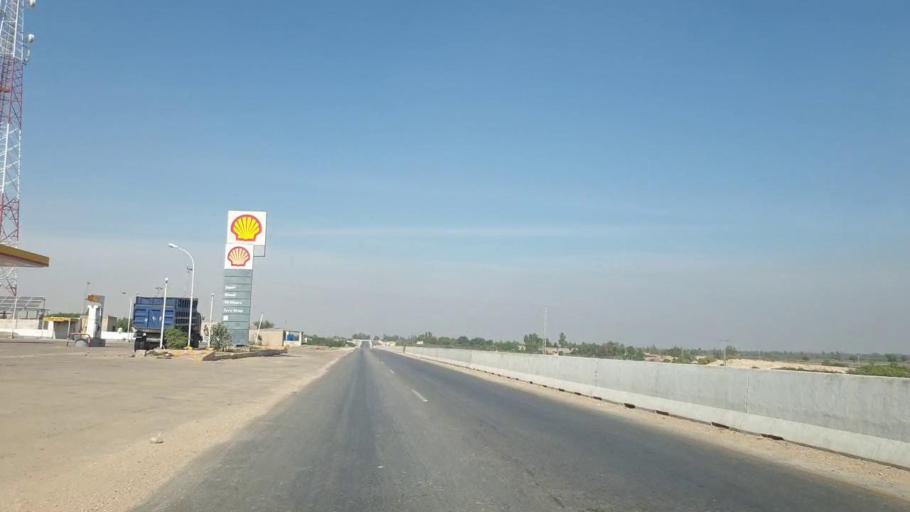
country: PK
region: Sindh
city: Hala
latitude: 25.7048
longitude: 68.2957
